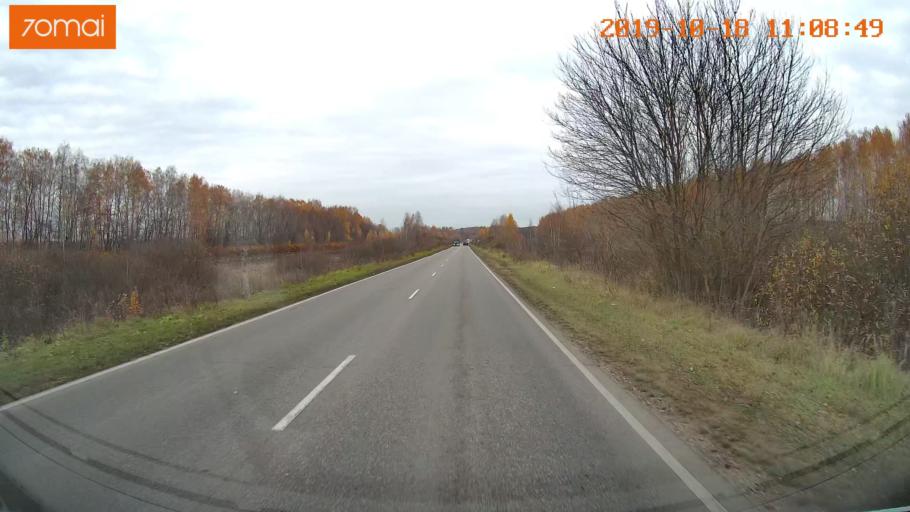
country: RU
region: Tula
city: Kimovsk
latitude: 53.9439
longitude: 38.5348
